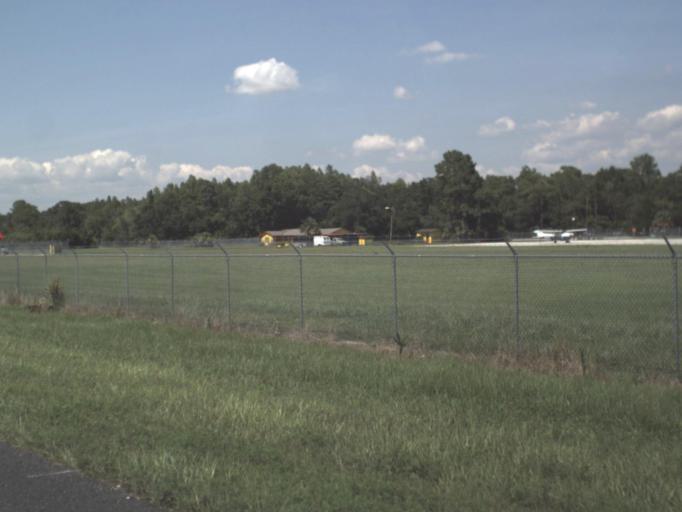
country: US
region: Florida
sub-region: Citrus County
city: Crystal River
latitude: 28.8708
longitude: -82.5796
